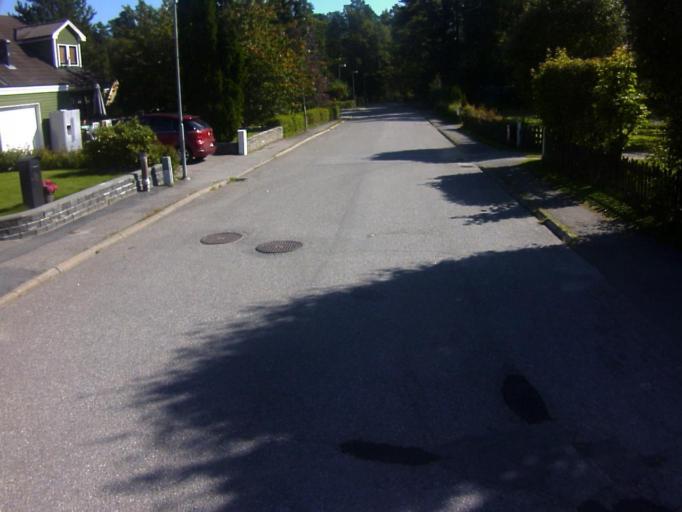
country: SE
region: Soedermanland
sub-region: Eskilstuna Kommun
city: Hallbybrunn
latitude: 59.3714
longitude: 16.4453
